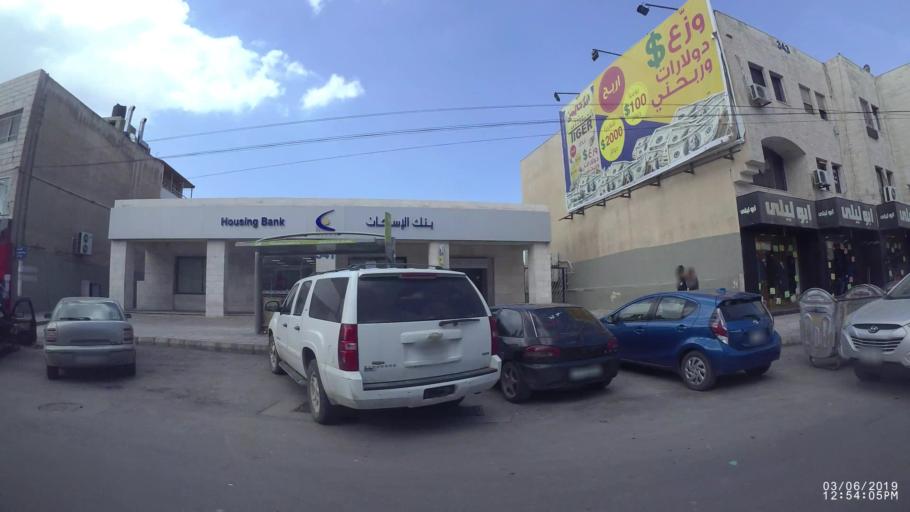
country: JO
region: Amman
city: Amman
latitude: 31.9796
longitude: 35.9843
